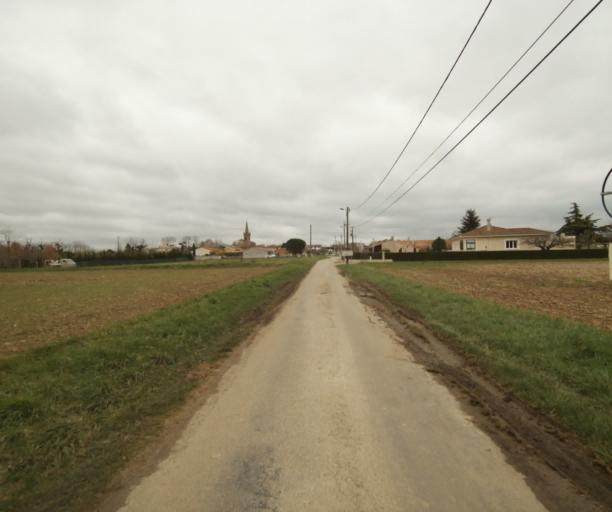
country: FR
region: Midi-Pyrenees
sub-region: Departement de l'Ariege
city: Pamiers
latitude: 43.1526
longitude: 1.6326
